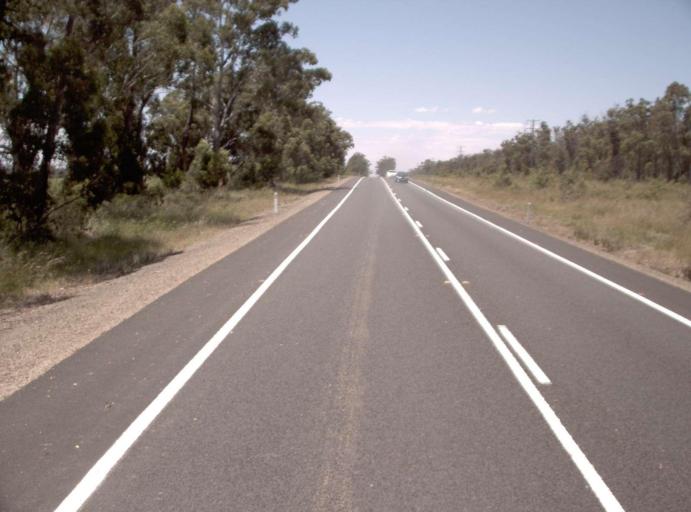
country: AU
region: Victoria
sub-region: East Gippsland
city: Lakes Entrance
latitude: -37.7551
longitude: 148.3115
